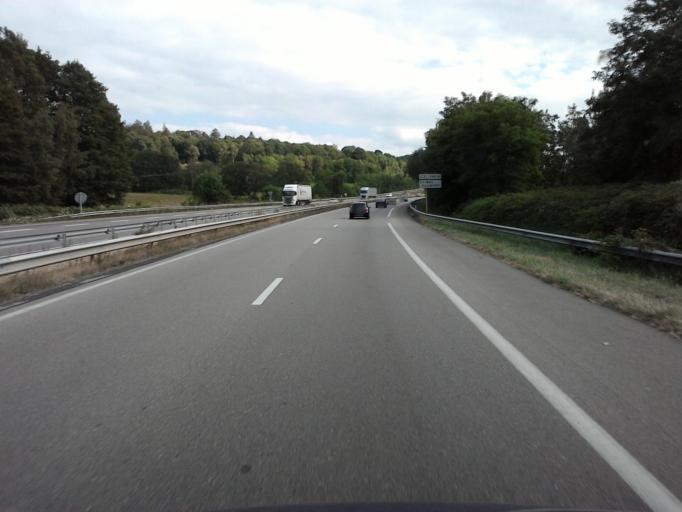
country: FR
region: Lorraine
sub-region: Departement des Vosges
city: Epinal
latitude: 48.1818
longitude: 6.4844
